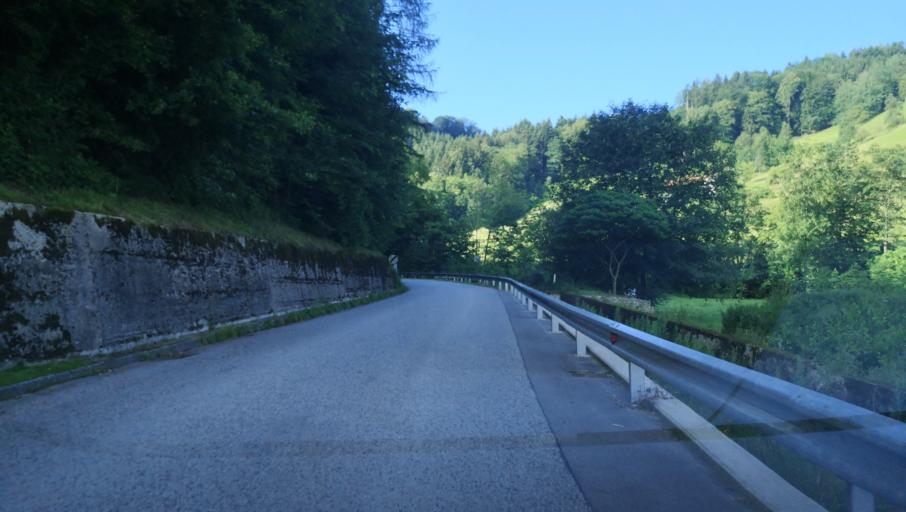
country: AT
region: Lower Austria
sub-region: Politischer Bezirk Scheibbs
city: Wang
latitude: 48.0201
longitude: 15.0379
